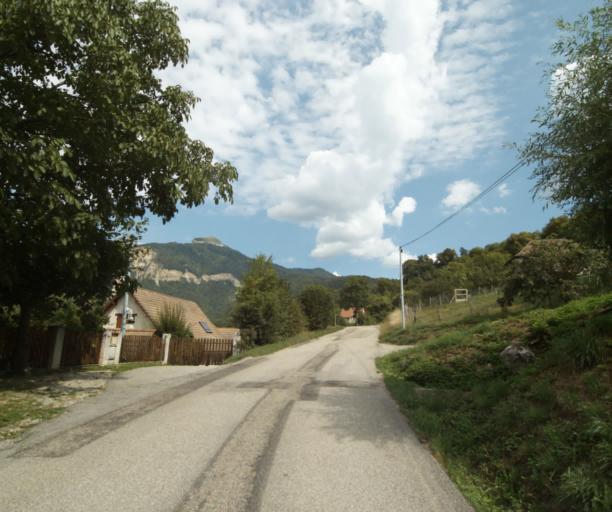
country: FR
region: Rhone-Alpes
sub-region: Departement de l'Isere
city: Le Sappey-en-Chartreuse
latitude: 45.2560
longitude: 5.7429
